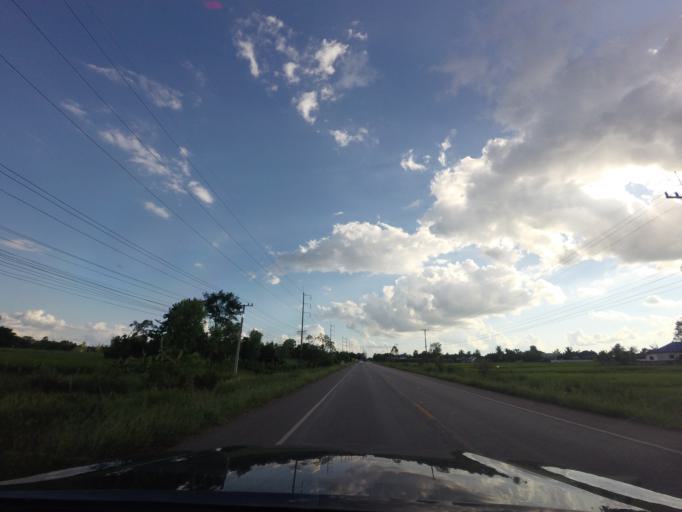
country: TH
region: Changwat Udon Thani
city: Thung Fon
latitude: 17.4601
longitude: 103.1890
